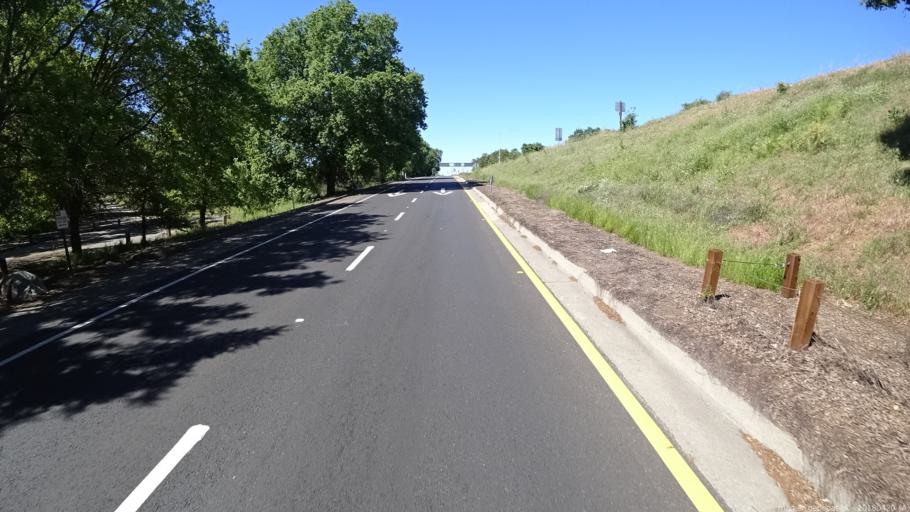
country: US
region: California
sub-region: Sacramento County
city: Sacramento
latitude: 38.5974
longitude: -121.4731
